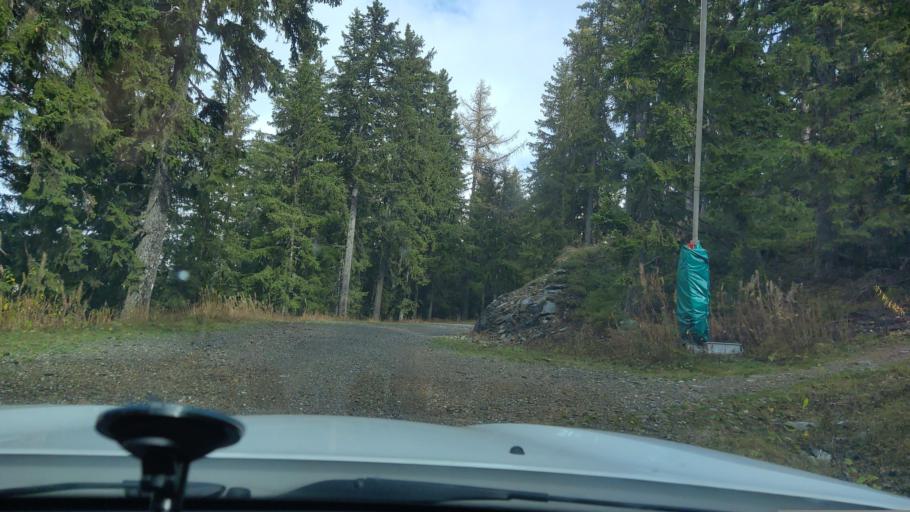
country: FR
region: Rhone-Alpes
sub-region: Departement de la Savoie
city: Seez
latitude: 45.5982
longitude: 6.8007
